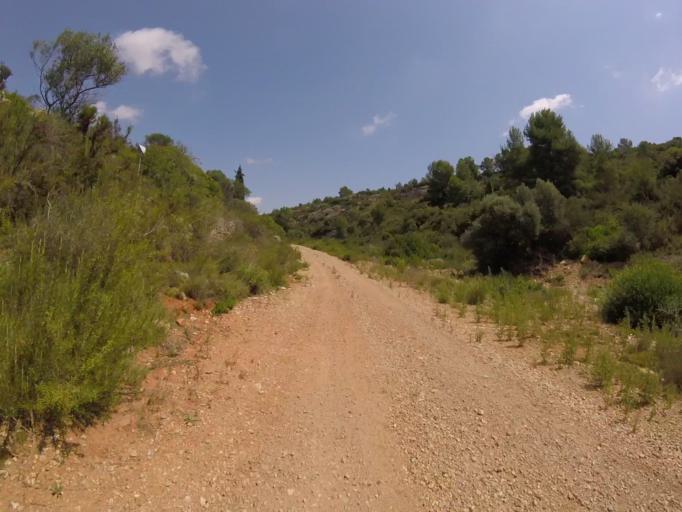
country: ES
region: Valencia
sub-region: Provincia de Castello
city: Torreblanca
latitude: 40.2087
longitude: 0.1399
